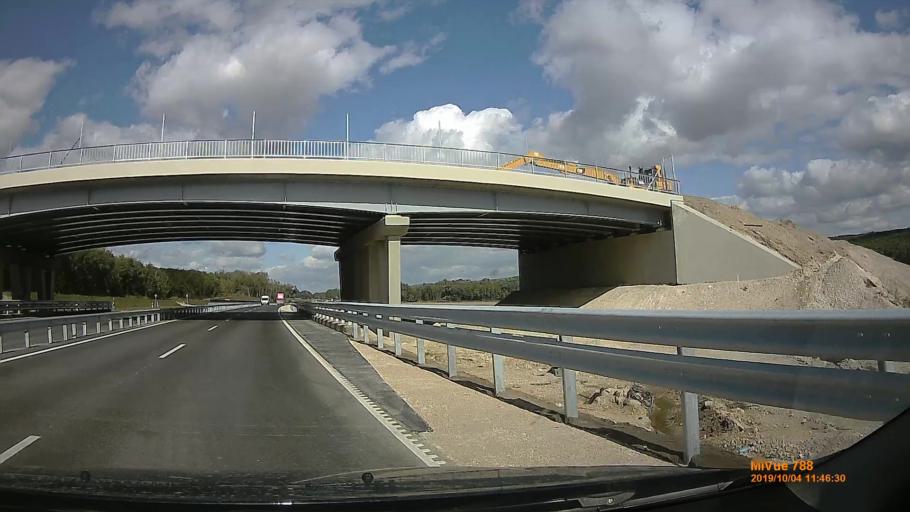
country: HU
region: Somogy
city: Karad
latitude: 46.6373
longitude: 17.7889
